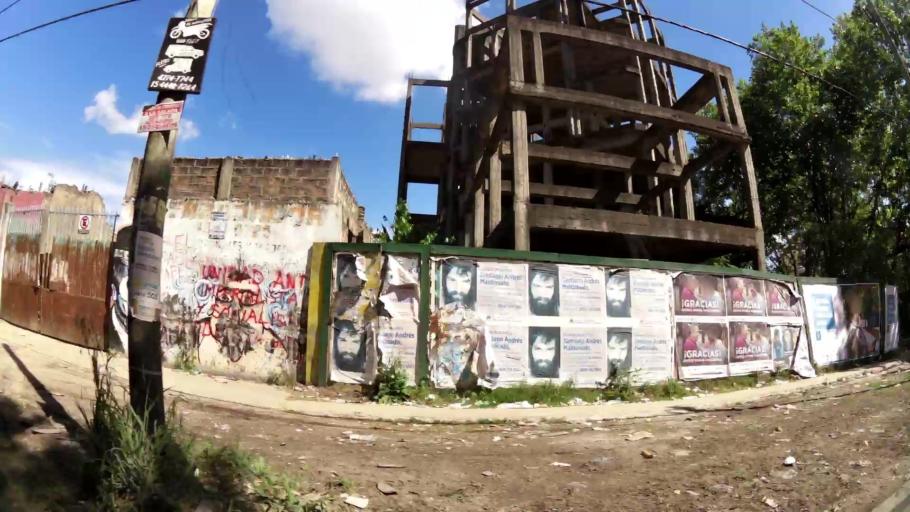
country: AR
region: Buenos Aires
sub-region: Partido de Quilmes
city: Quilmes
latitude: -34.8118
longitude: -58.2741
